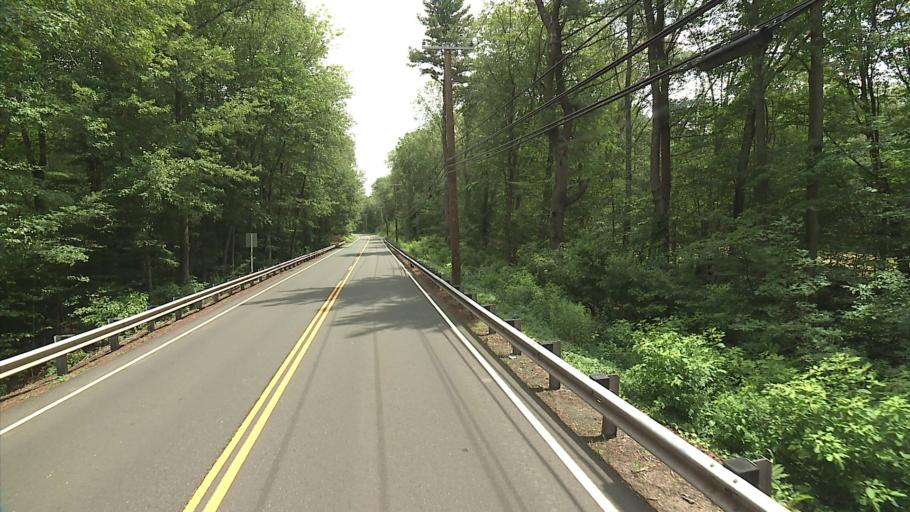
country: US
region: Connecticut
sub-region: New Haven County
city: Madison Center
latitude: 41.3580
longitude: -72.6203
